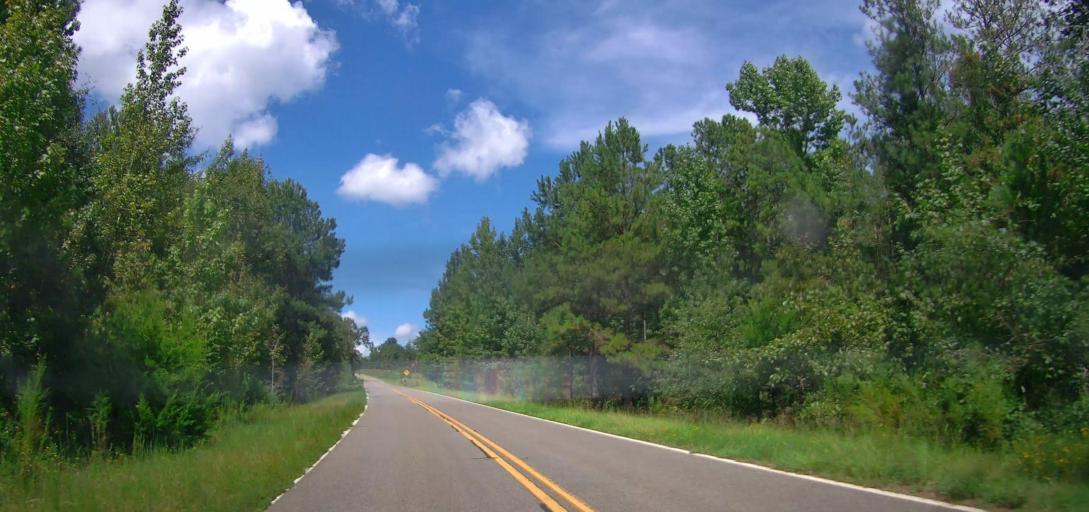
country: US
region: Georgia
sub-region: Peach County
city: Fort Valley
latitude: 32.5106
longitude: -83.8285
